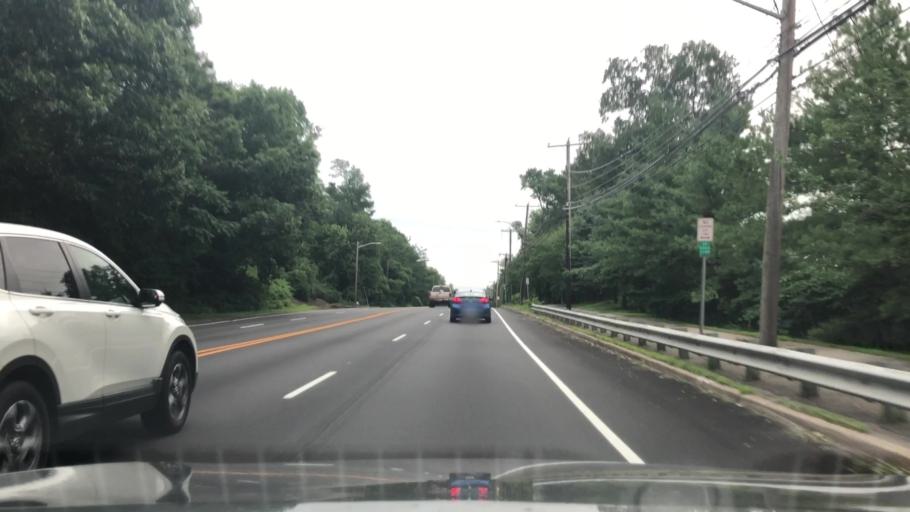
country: US
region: New York
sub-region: Nassau County
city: Woodbury
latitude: 40.8132
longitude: -73.4833
